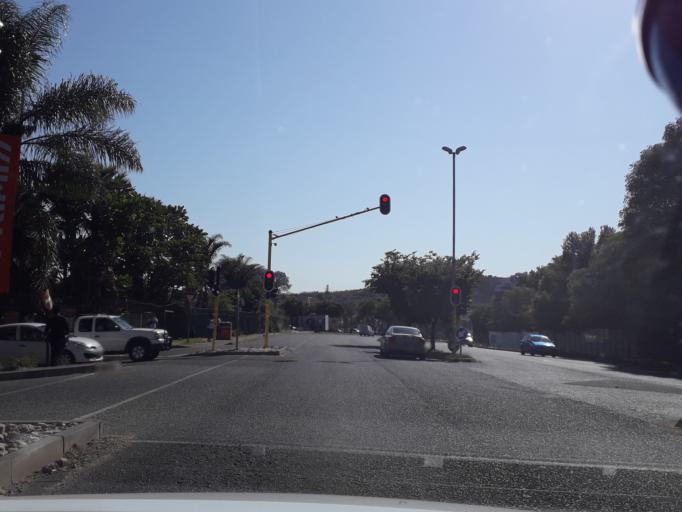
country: ZA
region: Gauteng
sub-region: City of Johannesburg Metropolitan Municipality
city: Roodepoort
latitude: -26.0963
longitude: 27.9439
